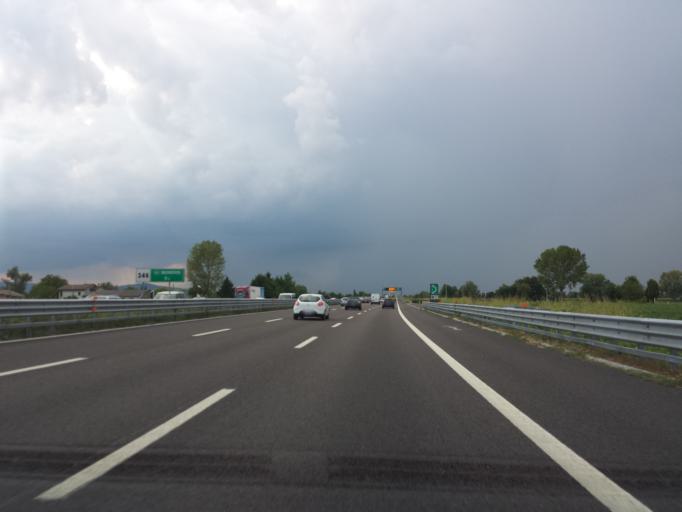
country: IT
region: Veneto
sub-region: Provincia di Padova
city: Arlesega
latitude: 45.4697
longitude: 11.7337
